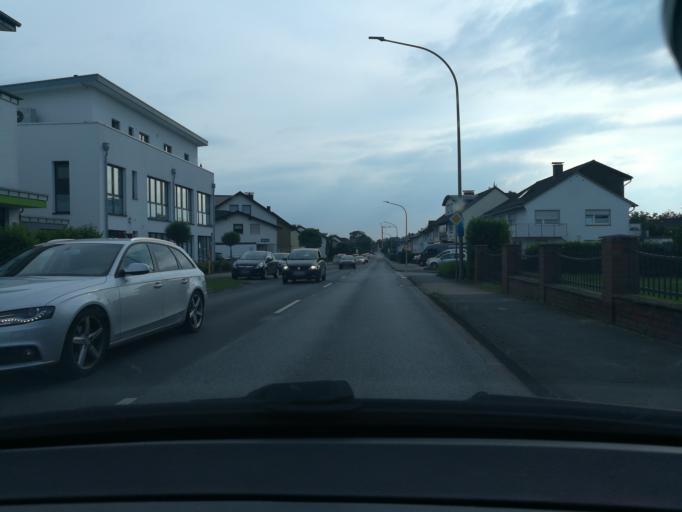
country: DE
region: North Rhine-Westphalia
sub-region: Regierungsbezirk Detmold
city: Oerlinghausen
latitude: 51.9075
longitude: 8.6494
